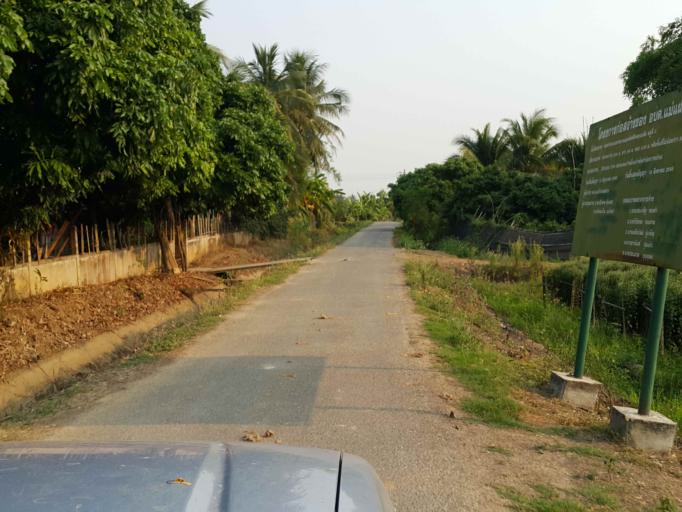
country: TH
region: Chiang Mai
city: Mae Taeng
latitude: 19.0465
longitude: 98.9705
